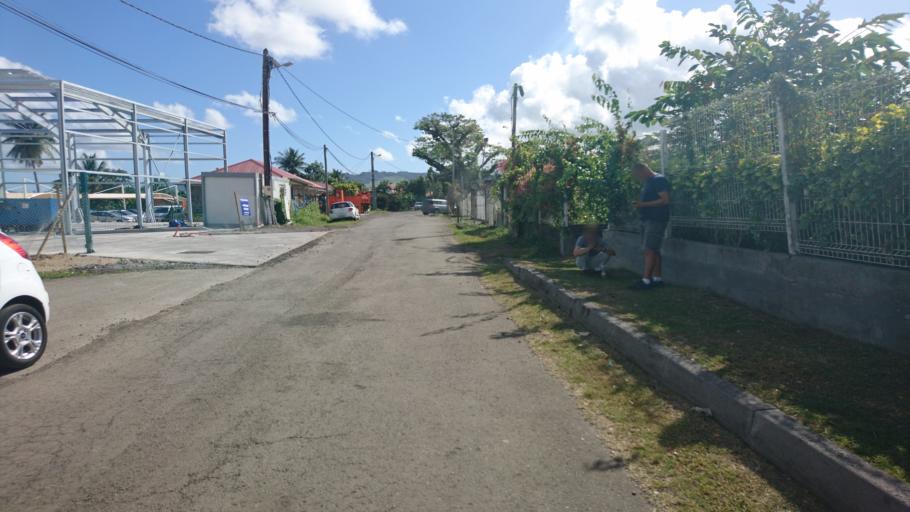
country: MQ
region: Martinique
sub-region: Martinique
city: Le Lamentin
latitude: 14.5981
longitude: -60.9959
